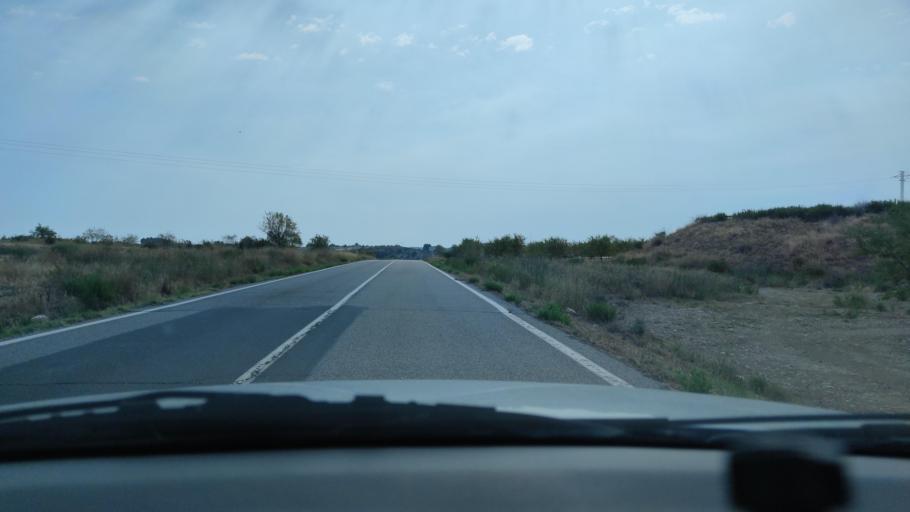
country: ES
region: Catalonia
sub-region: Provincia de Lleida
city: Arbeca
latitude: 41.5027
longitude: 0.9493
